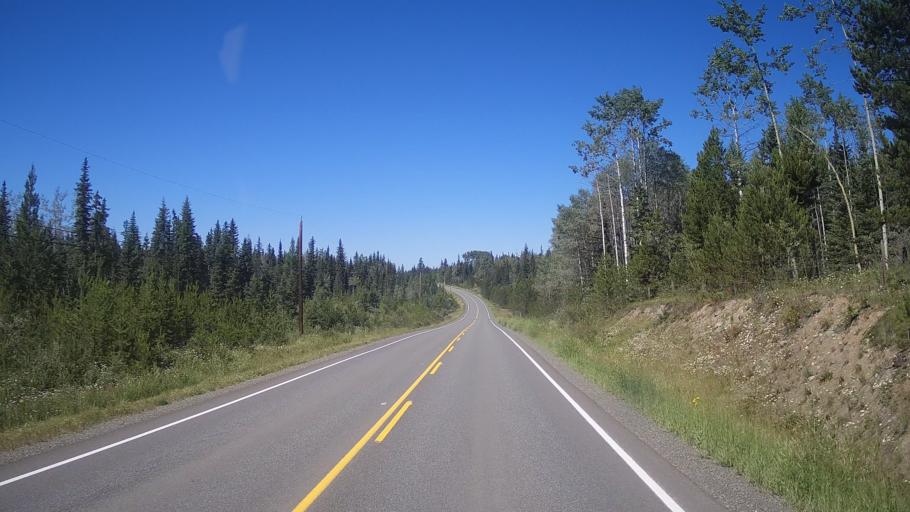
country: CA
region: British Columbia
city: Cache Creek
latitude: 51.5427
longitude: -120.9623
